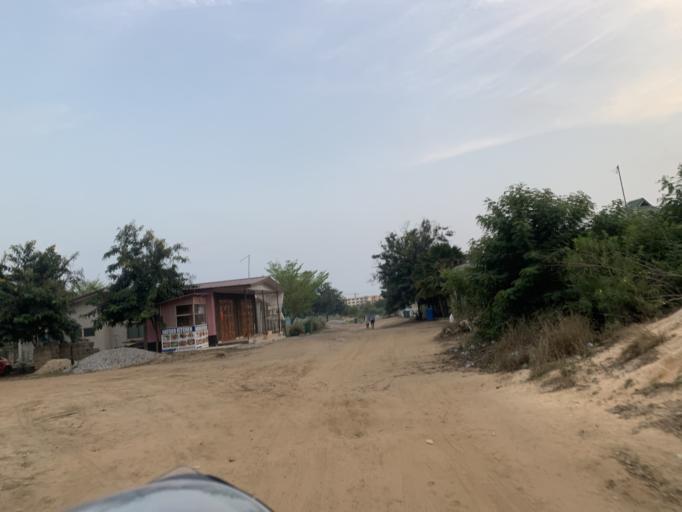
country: GH
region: Central
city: Winneba
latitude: 5.3767
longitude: -0.6321
